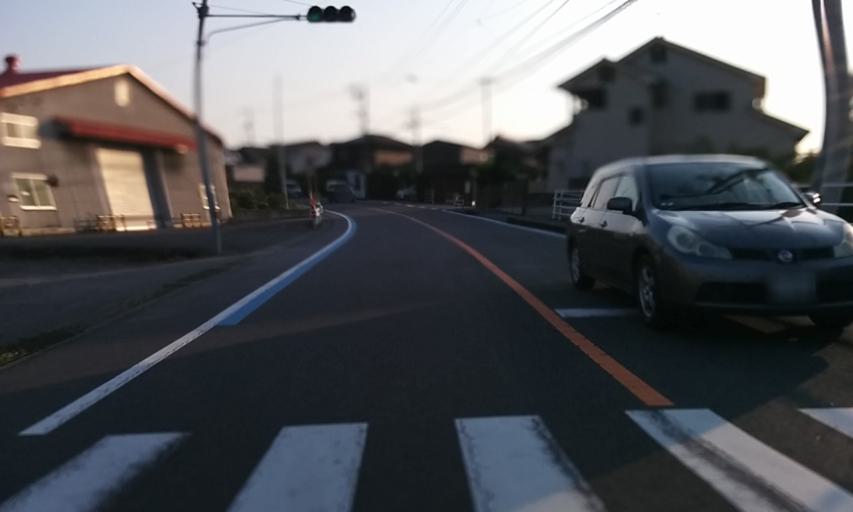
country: JP
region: Ehime
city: Masaki-cho
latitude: 33.7810
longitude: 132.7589
